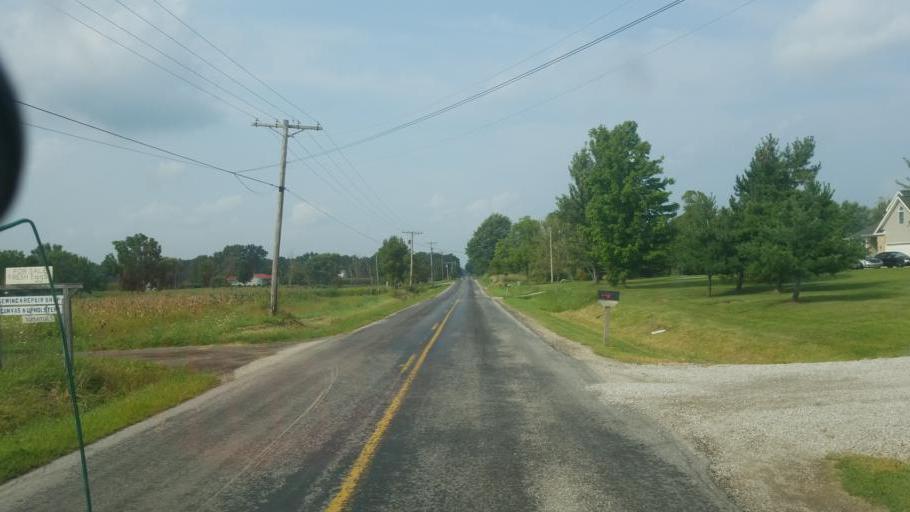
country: US
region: Ohio
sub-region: Lorain County
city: Wellington
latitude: 41.0722
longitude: -82.1620
